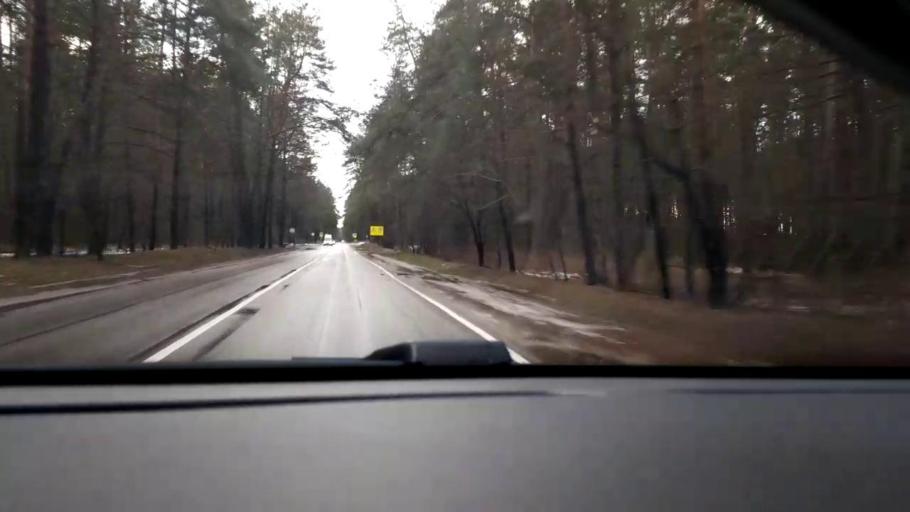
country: LT
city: Nemencine
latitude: 54.7847
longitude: 25.3836
